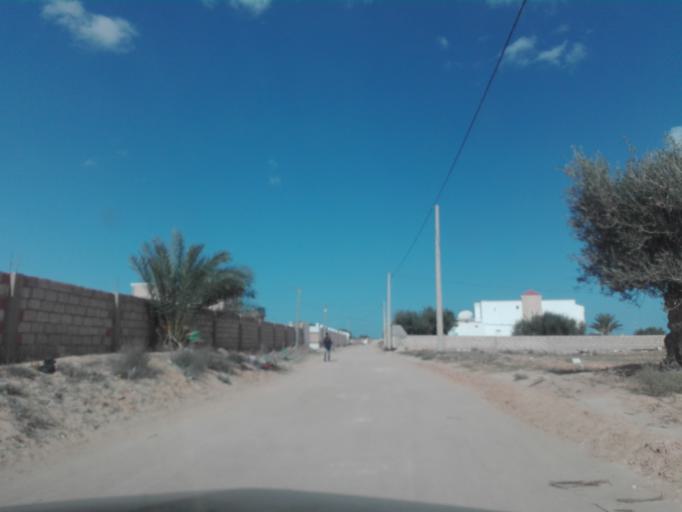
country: TN
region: Madanin
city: Bin Qirdan
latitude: 33.1607
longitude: 11.1951
